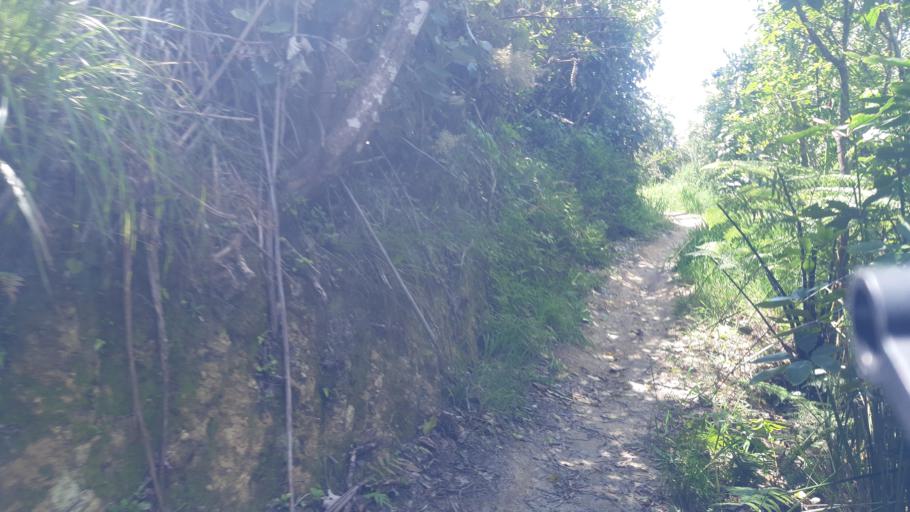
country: NZ
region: Marlborough
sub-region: Marlborough District
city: Picton
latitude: -41.2669
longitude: 174.0304
